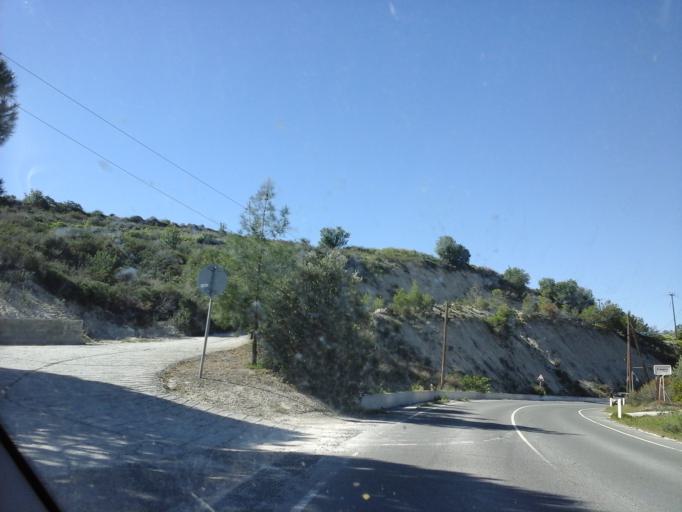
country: CY
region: Limassol
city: Pelendri
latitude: 34.8300
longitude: 32.9165
